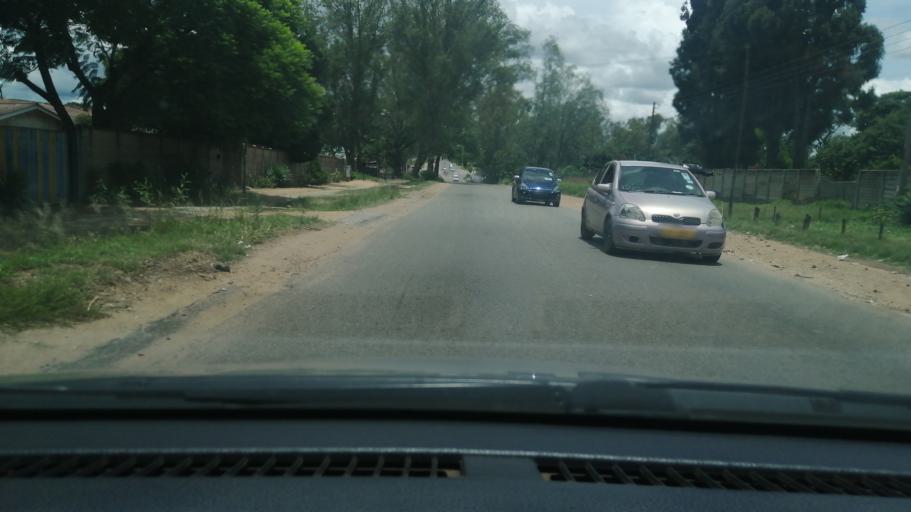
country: ZW
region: Harare
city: Harare
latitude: -17.8829
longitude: 31.0774
